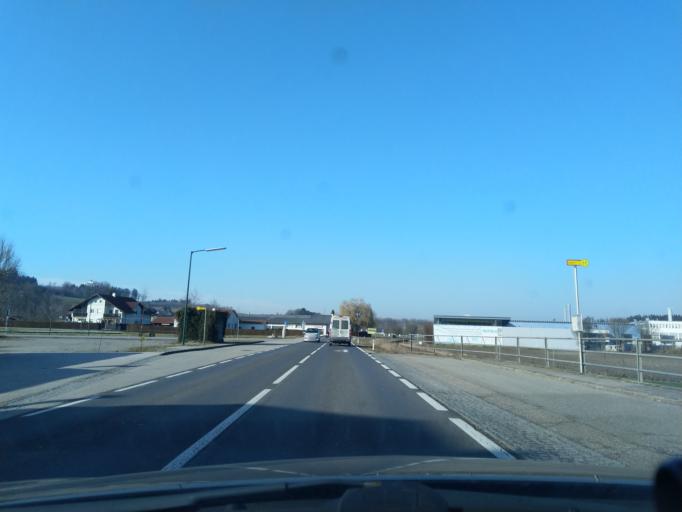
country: AT
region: Upper Austria
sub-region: Politischer Bezirk Ried im Innkreis
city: Ried im Innkreis
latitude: 48.2321
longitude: 13.4667
